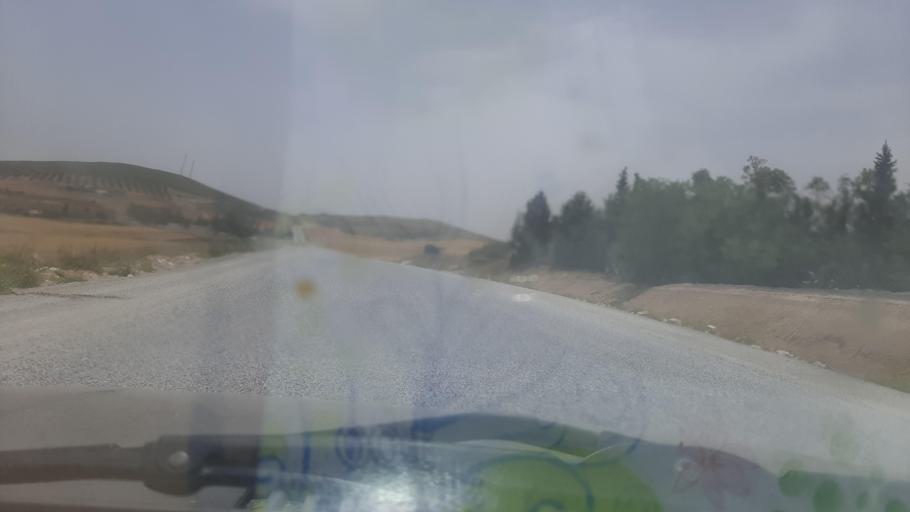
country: TN
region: Tunis
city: La Mohammedia
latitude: 36.5433
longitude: 10.1513
